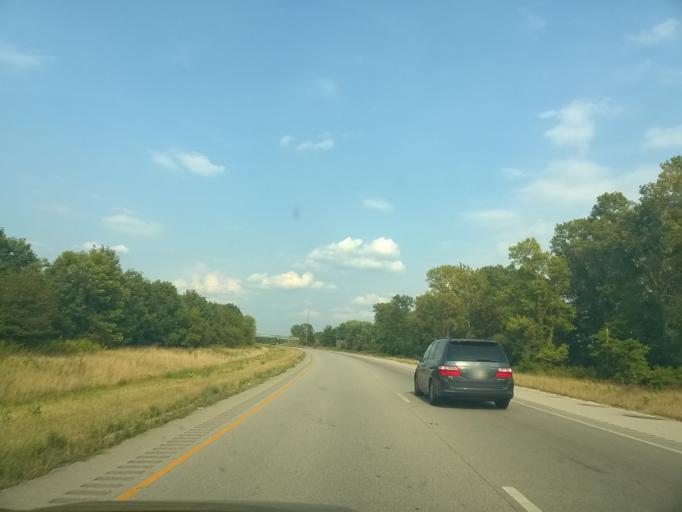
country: US
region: Indiana
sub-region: Vigo County
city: Seelyville
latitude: 39.4307
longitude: -87.2984
